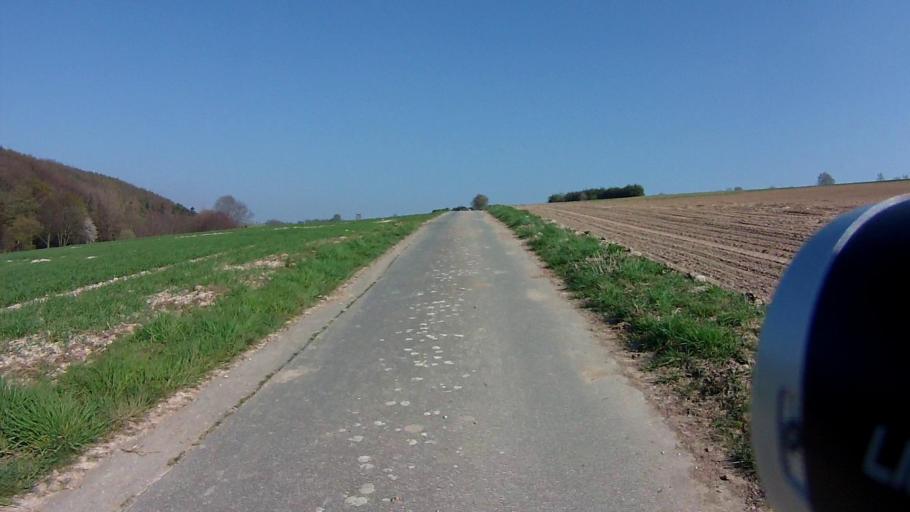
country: DE
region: North Rhine-Westphalia
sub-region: Regierungsbezirk Detmold
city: Paderborn
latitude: 51.7021
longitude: 8.8059
